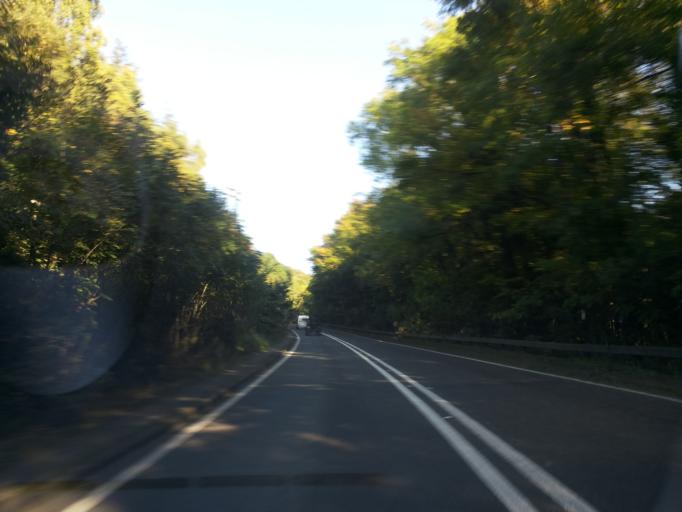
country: GB
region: England
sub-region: Derbyshire
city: Bakewell
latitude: 53.2460
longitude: -1.5947
